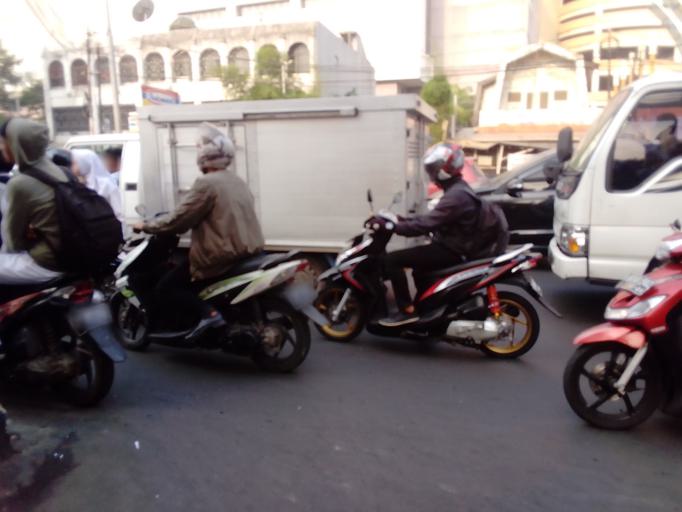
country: ID
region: Jakarta Raya
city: Jakarta
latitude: -6.1947
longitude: 106.8142
